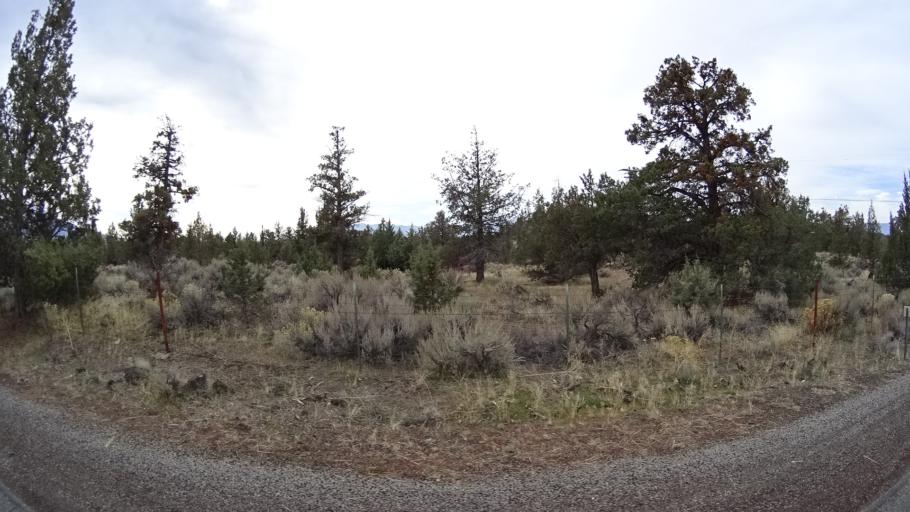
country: US
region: California
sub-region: Siskiyou County
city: Weed
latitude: 41.6034
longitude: -122.3547
